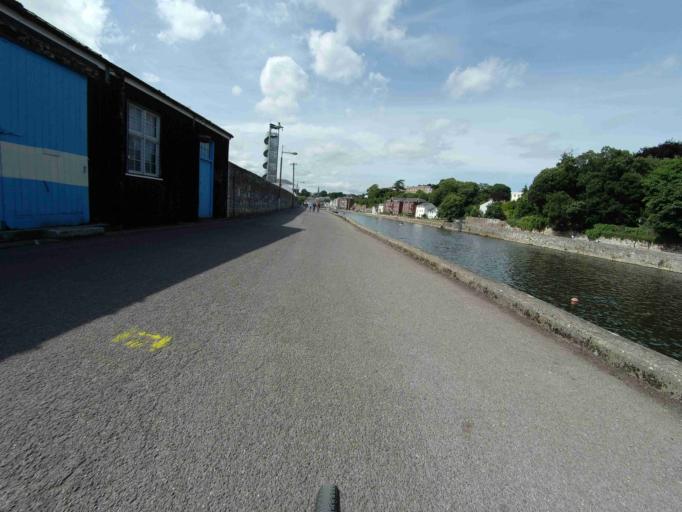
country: GB
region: England
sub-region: Devon
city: Exeter
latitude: 50.7157
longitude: -3.5277
